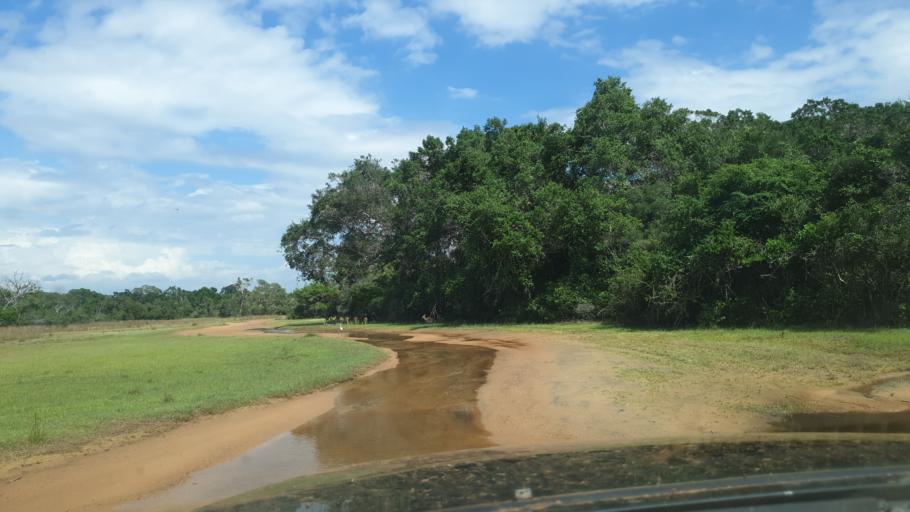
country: LK
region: North Central
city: Anuradhapura
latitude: 8.4246
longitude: 80.0127
